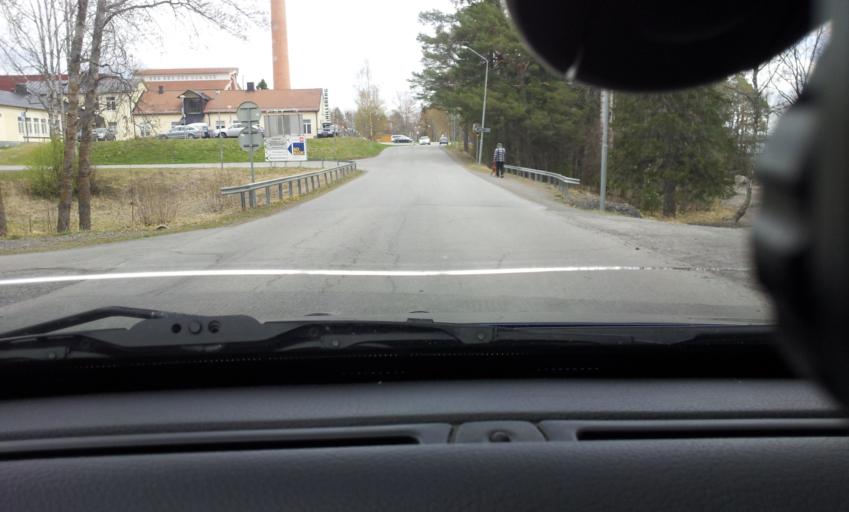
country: SE
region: Jaemtland
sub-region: OEstersunds Kommun
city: Ostersund
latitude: 63.1662
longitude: 14.5946
